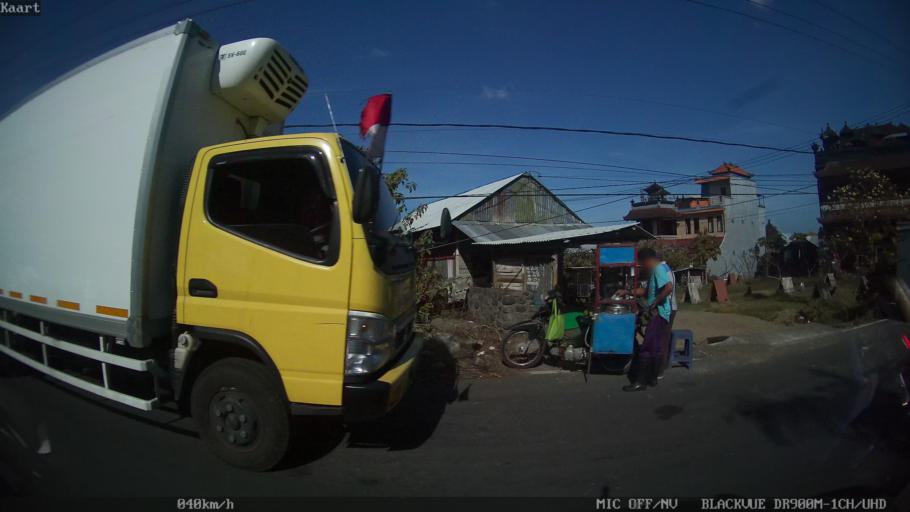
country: ID
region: Bali
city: Banjar Karangsuling
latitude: -8.6203
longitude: 115.1880
